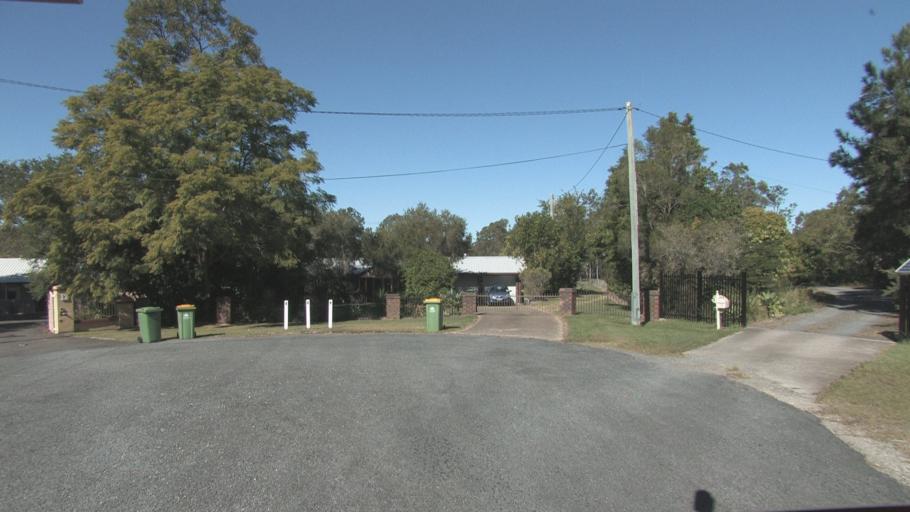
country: AU
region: Queensland
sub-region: Logan
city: Park Ridge South
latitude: -27.7237
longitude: 153.0556
